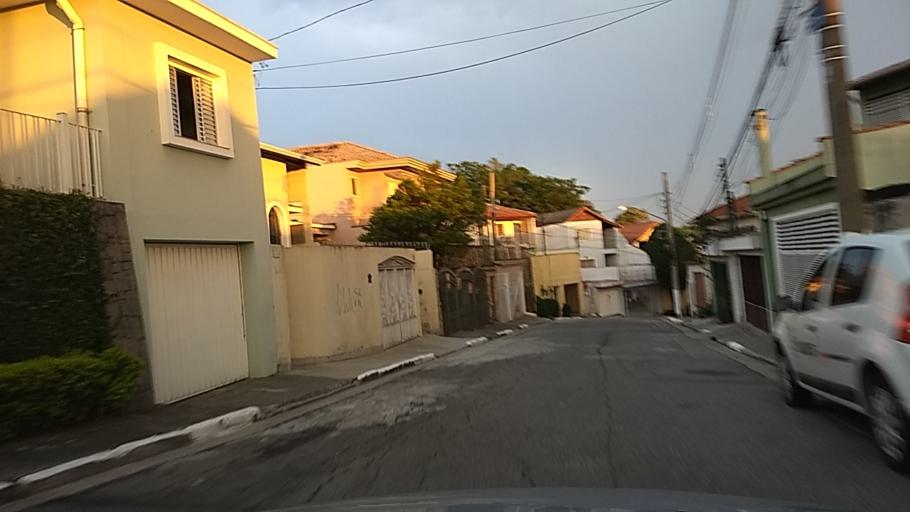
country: BR
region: Sao Paulo
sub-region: Osasco
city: Osasco
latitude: -23.4752
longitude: -46.7406
